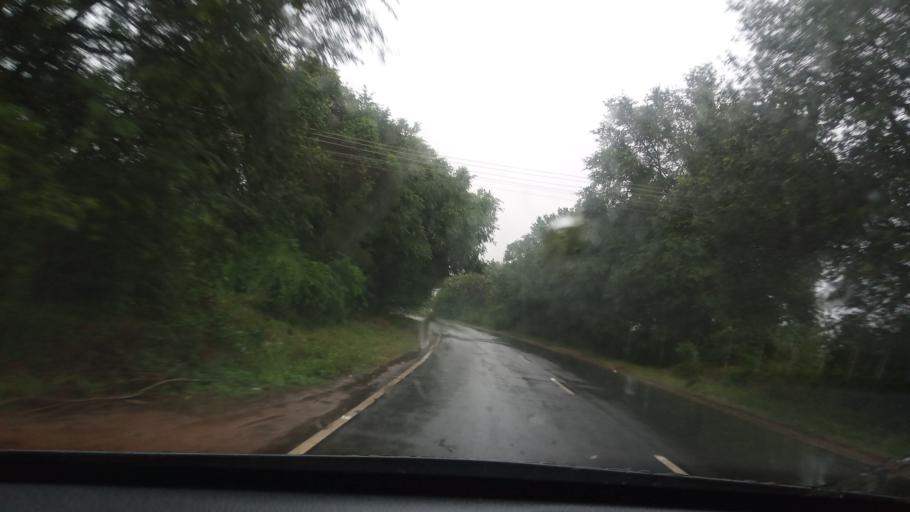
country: IN
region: Tamil Nadu
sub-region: Vellore
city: Kalavai
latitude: 12.8381
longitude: 79.4046
